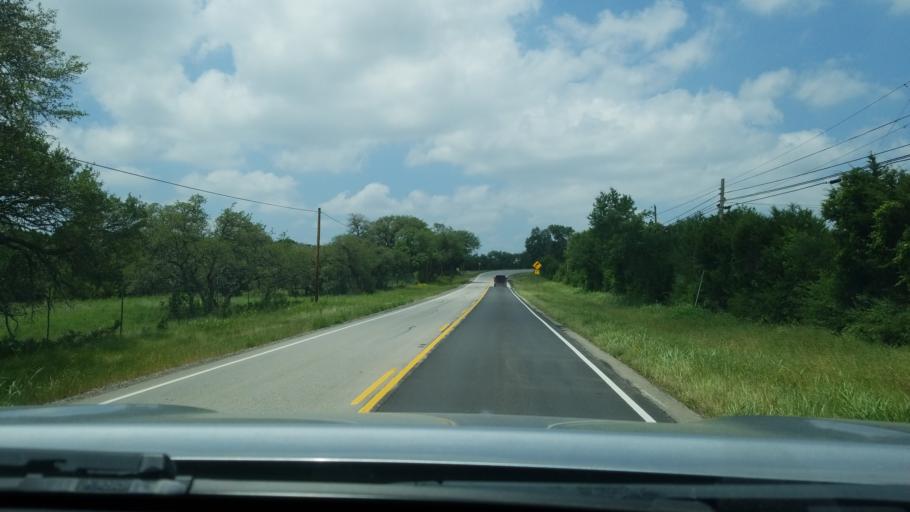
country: US
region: Texas
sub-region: Hays County
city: Dripping Springs
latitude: 30.1528
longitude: -98.0646
